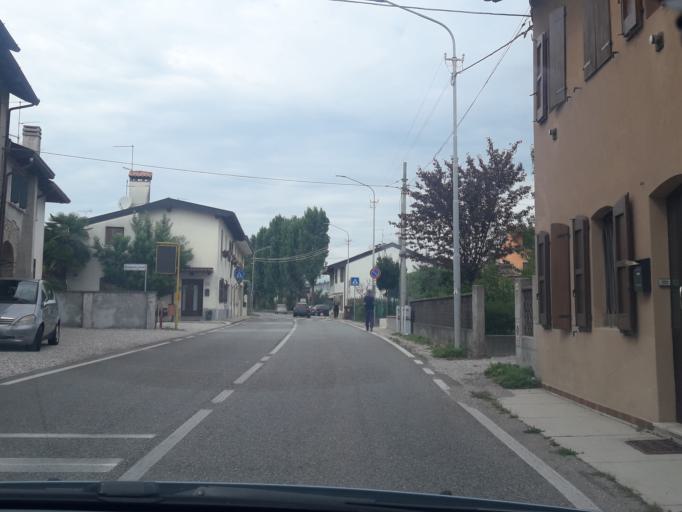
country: IT
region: Friuli Venezia Giulia
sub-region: Provincia di Udine
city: Udine
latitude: 46.0417
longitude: 13.2553
